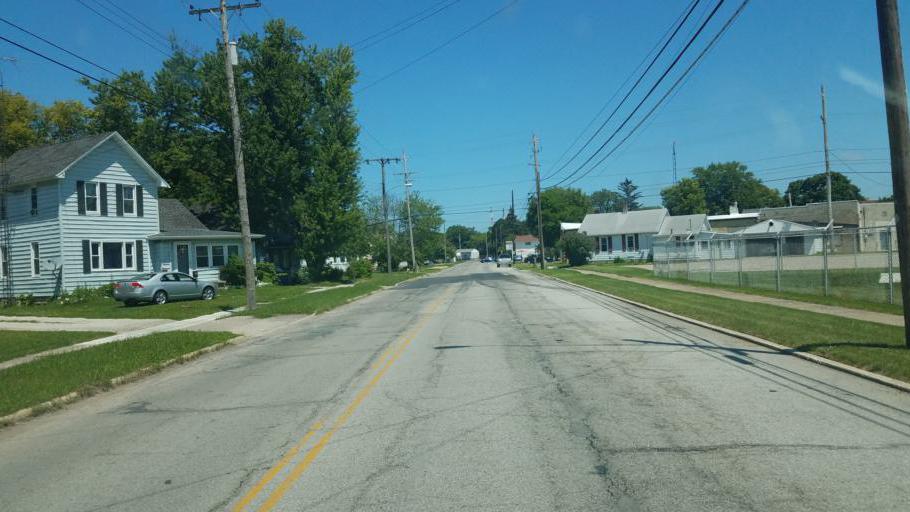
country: US
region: Ohio
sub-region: Ottawa County
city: Port Clinton
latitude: 41.5083
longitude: -82.9500
